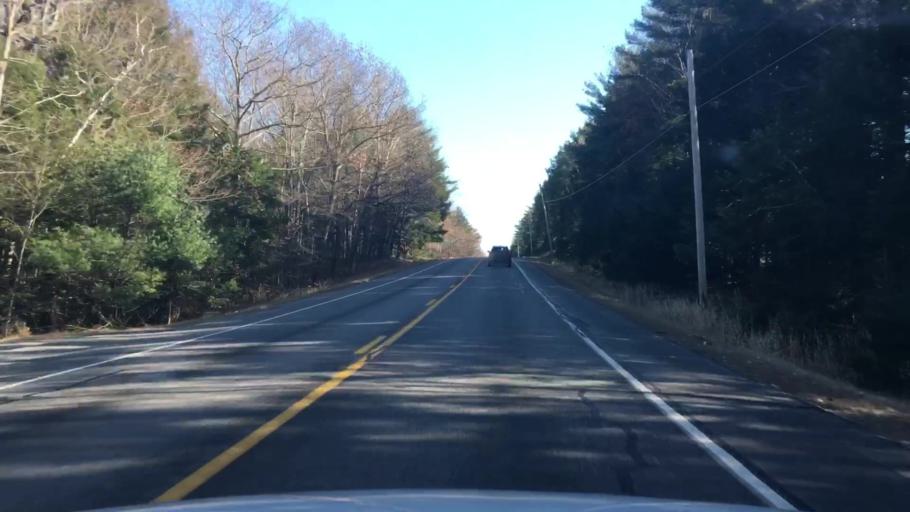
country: US
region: Maine
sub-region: Knox County
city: Washington
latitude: 44.2275
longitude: -69.3388
